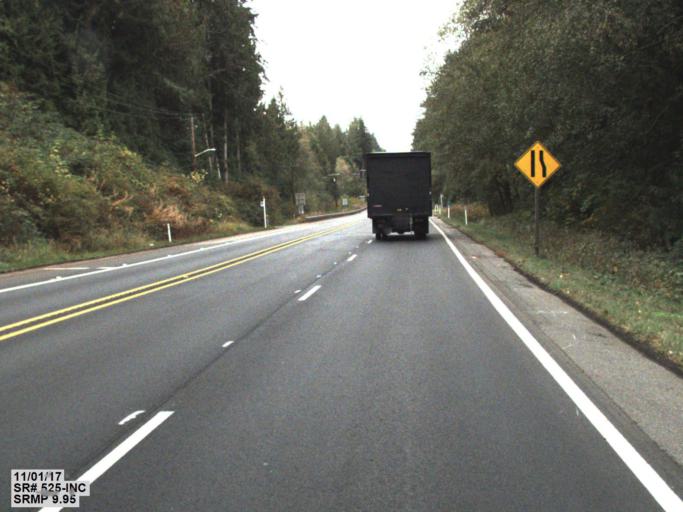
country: US
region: Washington
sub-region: Island County
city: Langley
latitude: 47.9796
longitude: -122.3793
